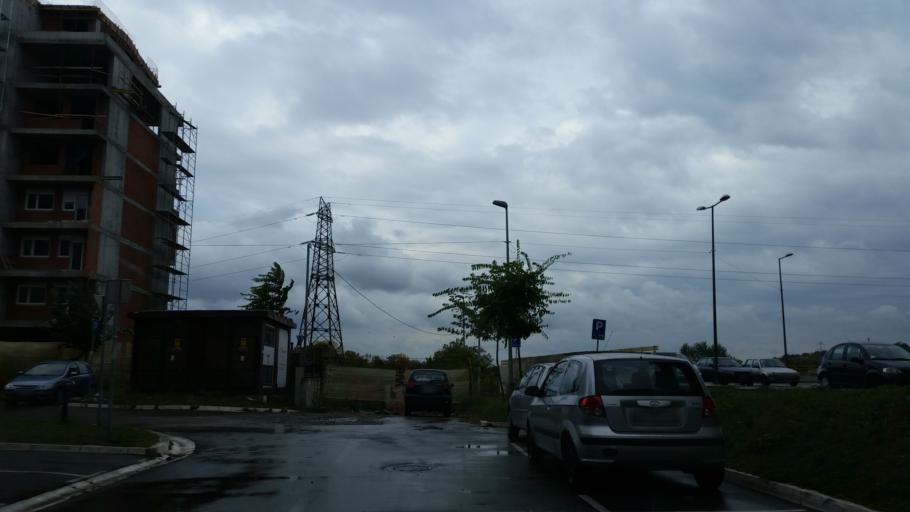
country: RS
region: Central Serbia
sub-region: Belgrade
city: Zemun
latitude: 44.7989
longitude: 20.3653
